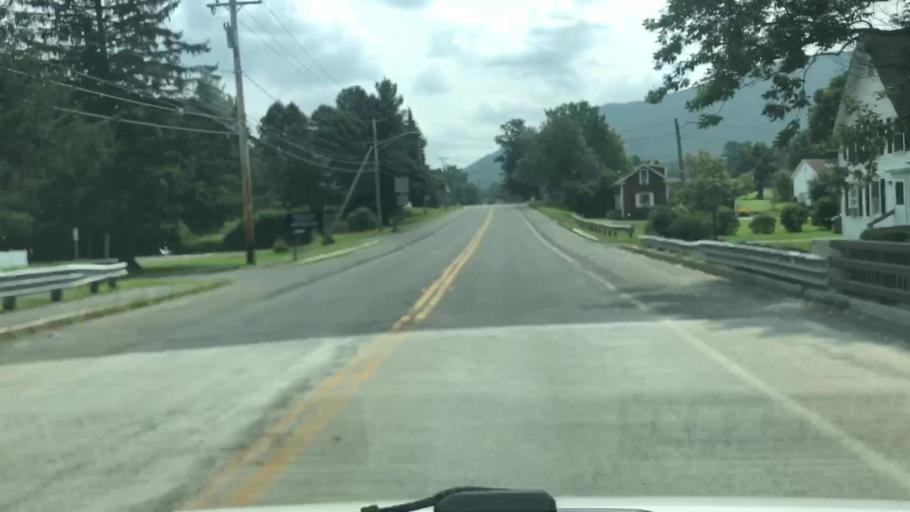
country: US
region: Massachusetts
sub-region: Berkshire County
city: Williamstown
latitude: 42.6601
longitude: -73.2414
